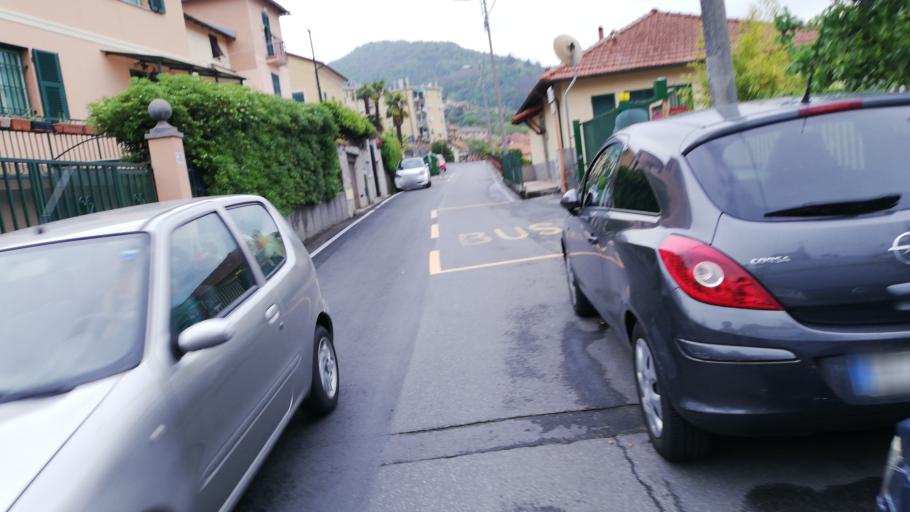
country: IT
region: Liguria
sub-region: Provincia di Genova
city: Piccarello
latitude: 44.4509
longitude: 9.0140
